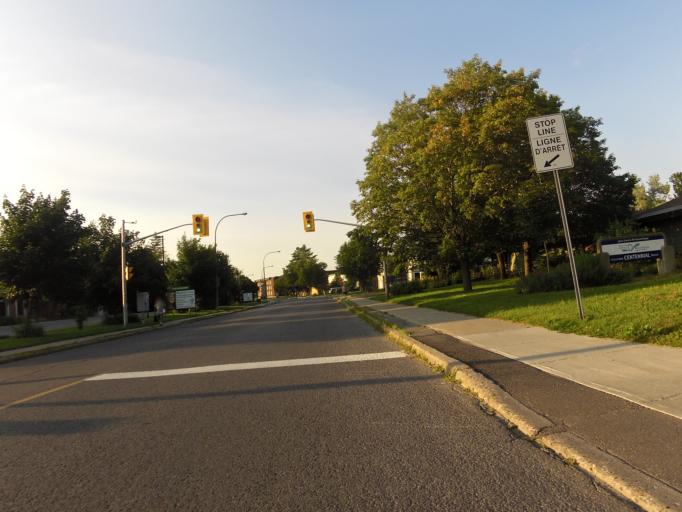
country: CA
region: Ontario
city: Bells Corners
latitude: 45.3207
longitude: -75.8263
